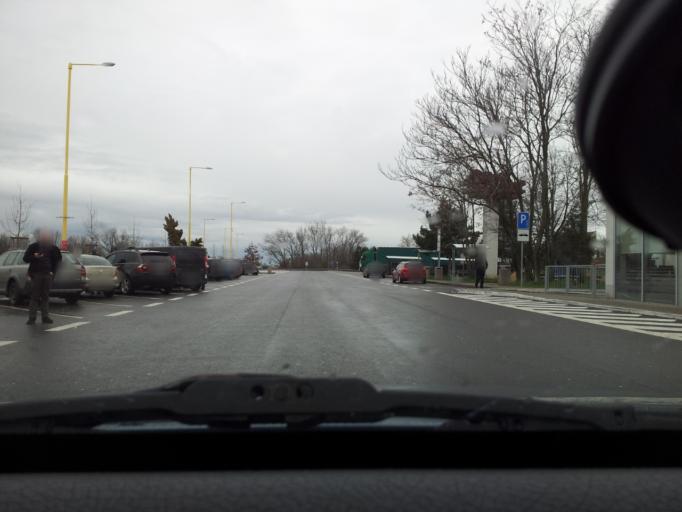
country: SK
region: Trnavsky
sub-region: Okres Trnava
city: Trnava
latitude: 48.3262
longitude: 17.6090
